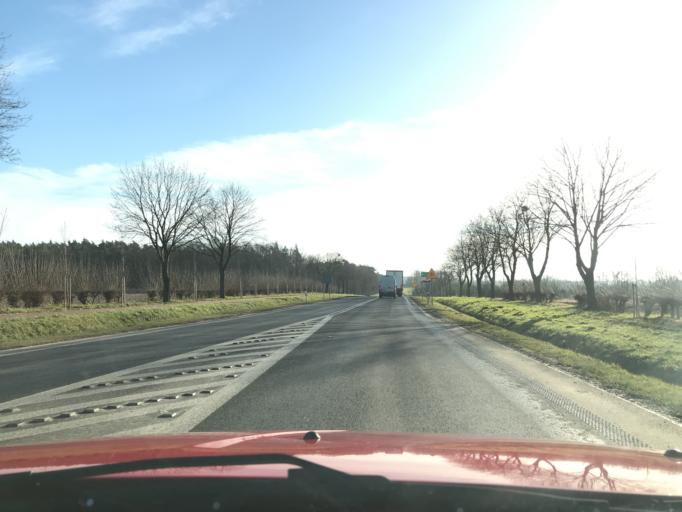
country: PL
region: Greater Poland Voivodeship
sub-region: Powiat pleszewski
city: Goluchow
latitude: 51.8635
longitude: 17.9045
